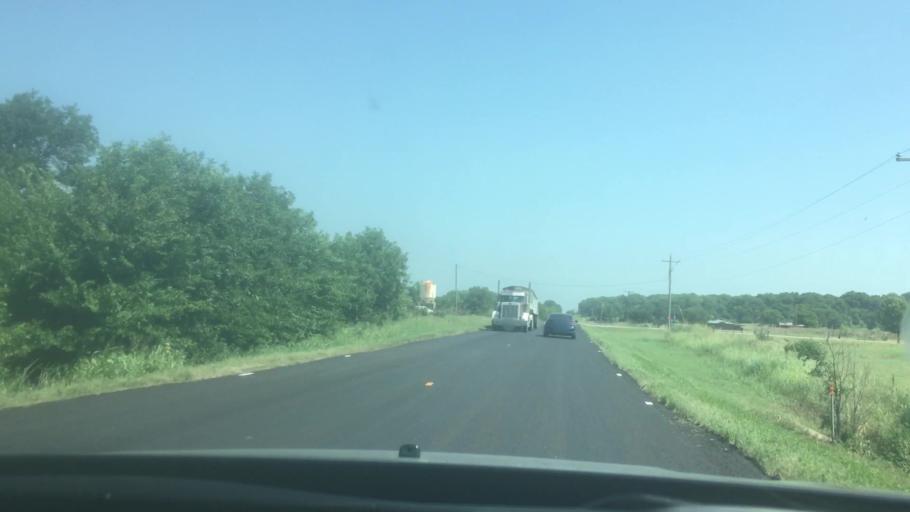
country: US
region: Oklahoma
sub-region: Coal County
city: Coalgate
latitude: 34.3568
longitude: -96.4243
